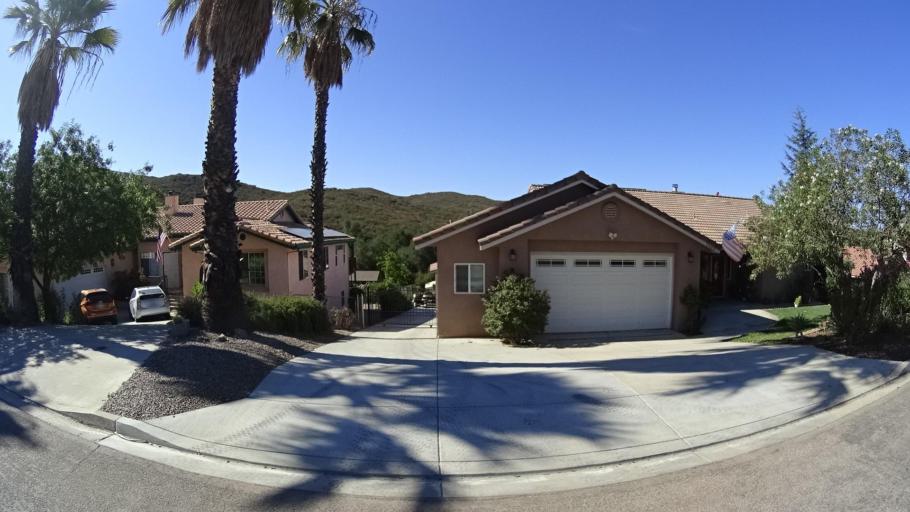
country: US
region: California
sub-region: San Diego County
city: San Diego Country Estates
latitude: 32.9999
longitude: -116.7655
